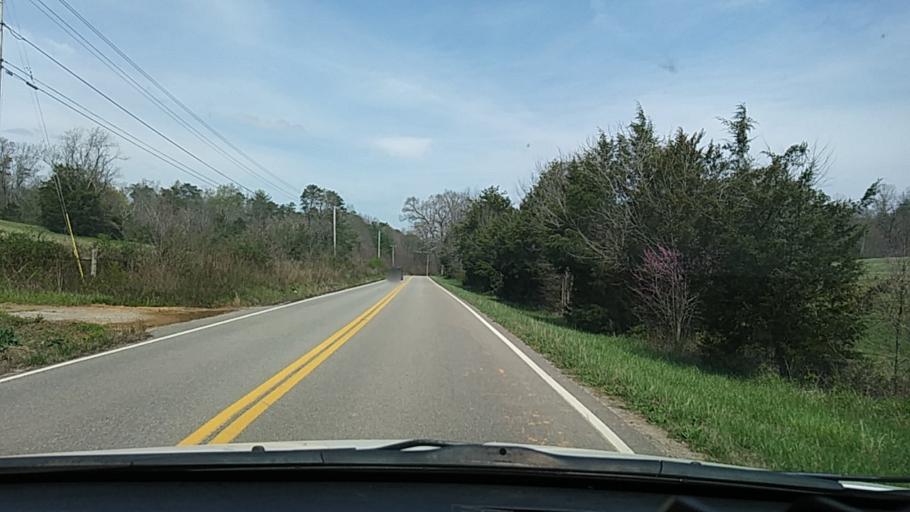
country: US
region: Tennessee
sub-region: Greene County
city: Greeneville
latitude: 36.0939
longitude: -82.7927
